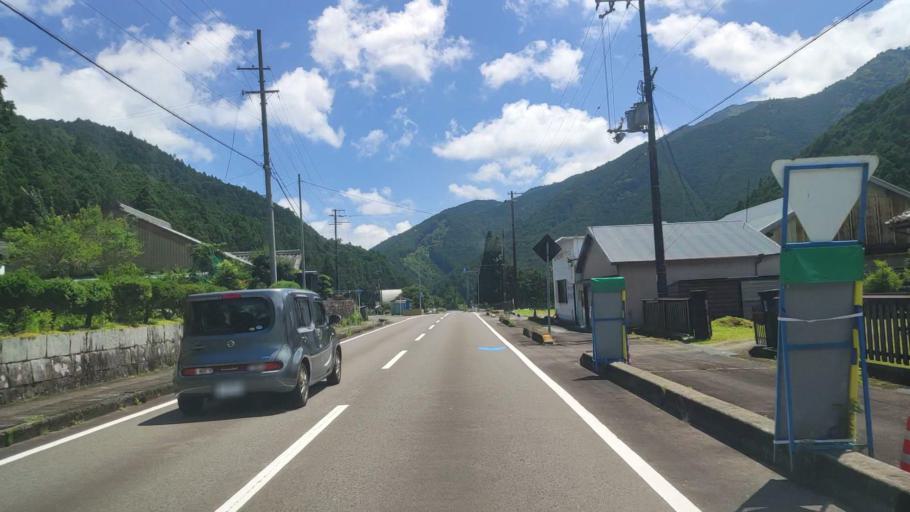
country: JP
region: Mie
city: Owase
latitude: 33.9787
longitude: 136.1046
